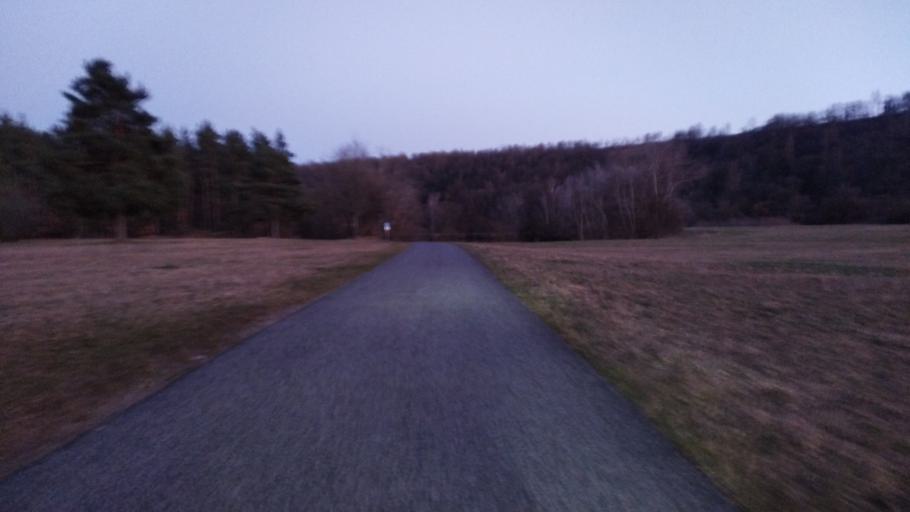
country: DE
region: Bavaria
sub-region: Regierungsbezirk Unterfranken
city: Nordheim
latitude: 49.8717
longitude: 10.1665
